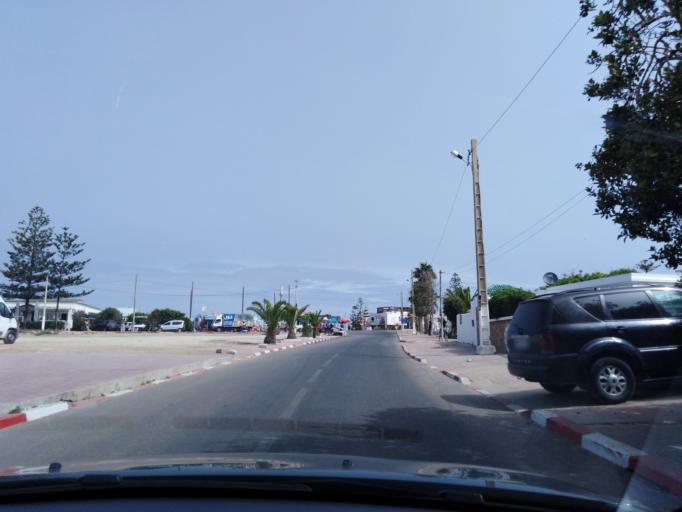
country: MA
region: Doukkala-Abda
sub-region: Safi
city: Safi
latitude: 32.7339
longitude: -9.0440
